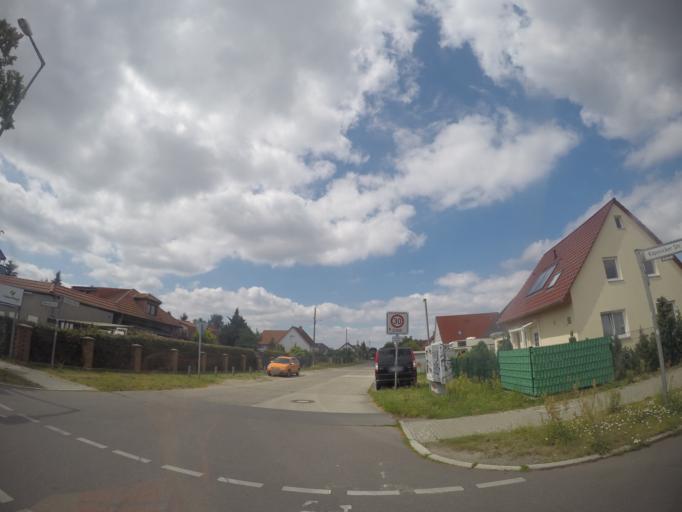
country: DE
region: Berlin
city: Biesdorf
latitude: 52.5015
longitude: 13.5615
